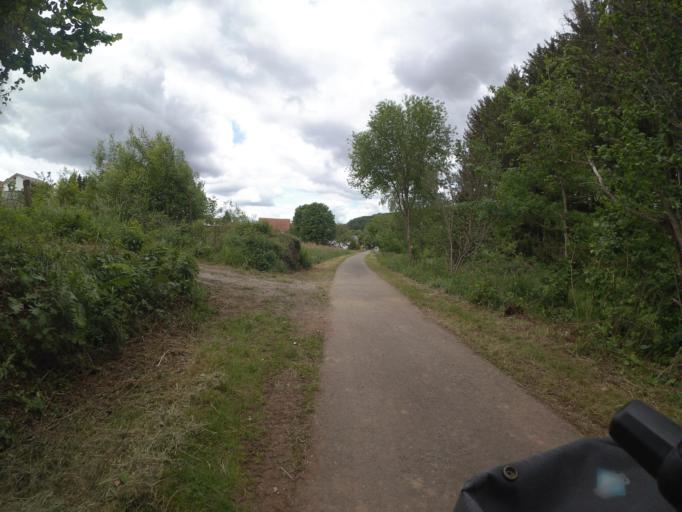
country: DE
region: Rheinland-Pfalz
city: Reichenbach-Steegen
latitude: 49.4979
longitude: 7.5460
